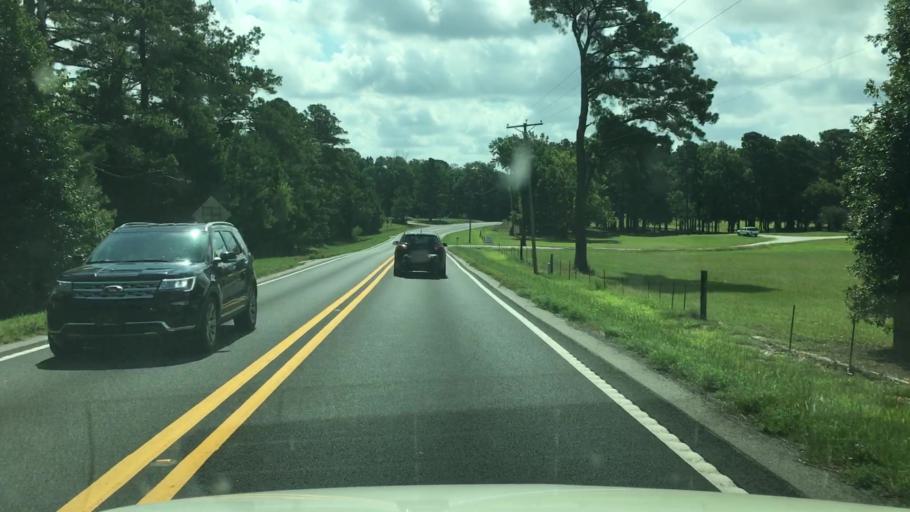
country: US
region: Arkansas
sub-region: Clark County
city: Arkadelphia
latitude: 34.2549
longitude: -93.1265
